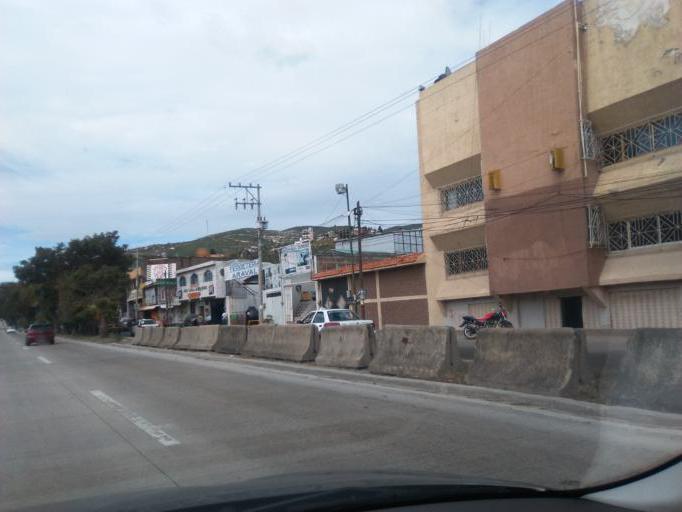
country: MX
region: Guerrero
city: Chilpancingo de los Bravos
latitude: 17.5599
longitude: -99.5101
